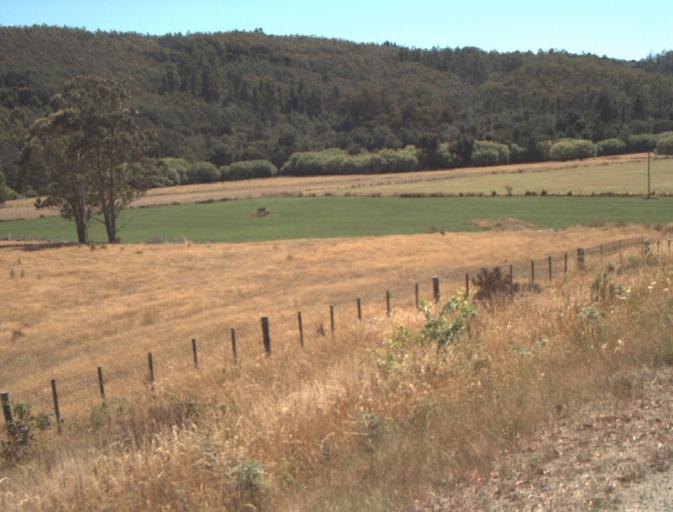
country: AU
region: Tasmania
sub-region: Dorset
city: Scottsdale
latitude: -41.3206
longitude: 147.3633
